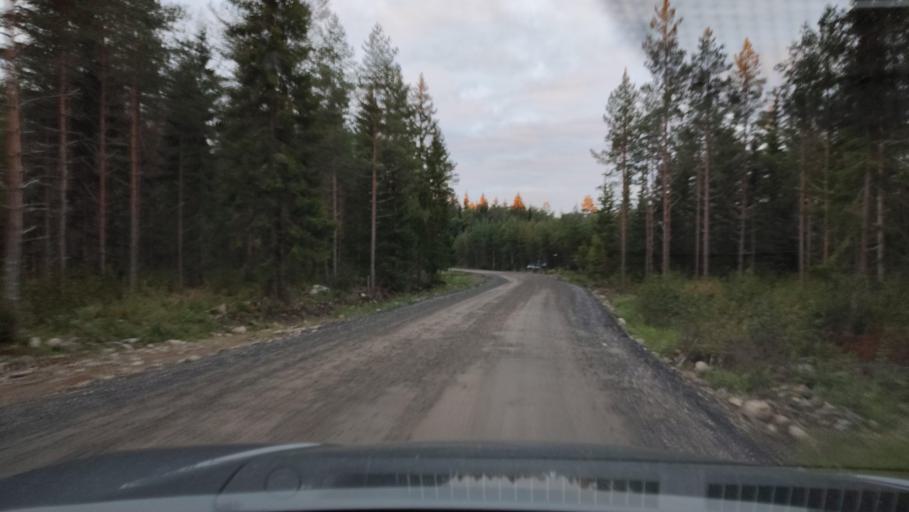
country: FI
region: Southern Ostrobothnia
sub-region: Suupohja
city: Karijoki
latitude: 62.1868
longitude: 21.5887
